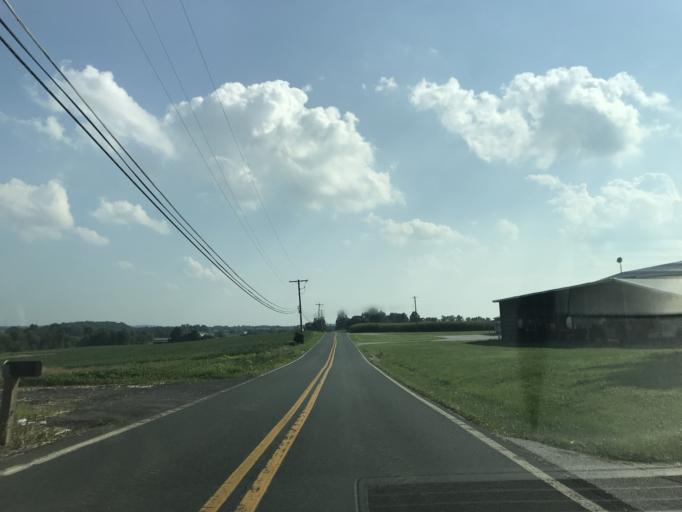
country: US
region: Maryland
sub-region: Carroll County
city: Westminster
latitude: 39.6184
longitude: -76.9786
